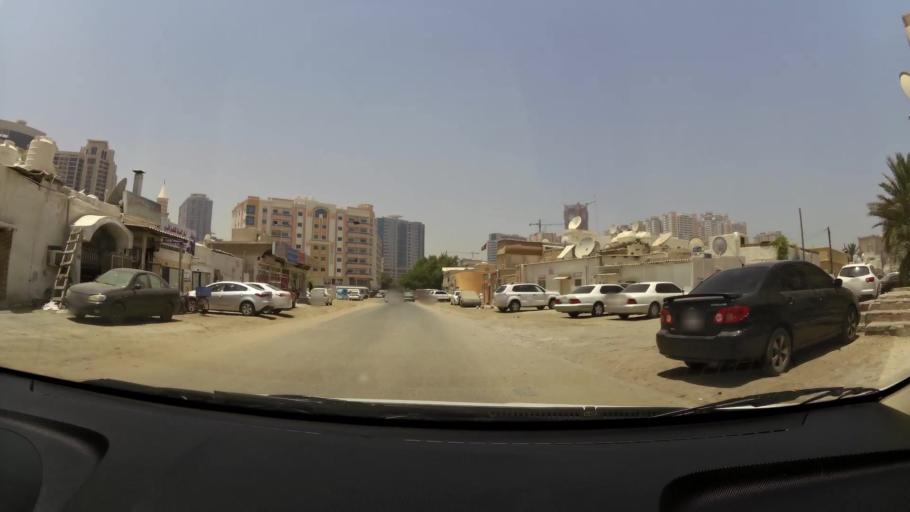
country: AE
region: Ajman
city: Ajman
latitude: 25.3963
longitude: 55.4390
